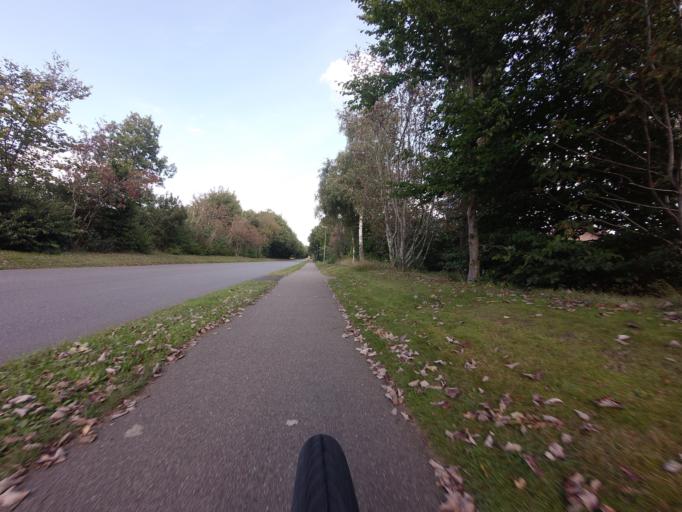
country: DK
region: Central Jutland
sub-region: Viborg Kommune
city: Karup
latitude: 56.3419
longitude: 9.2576
